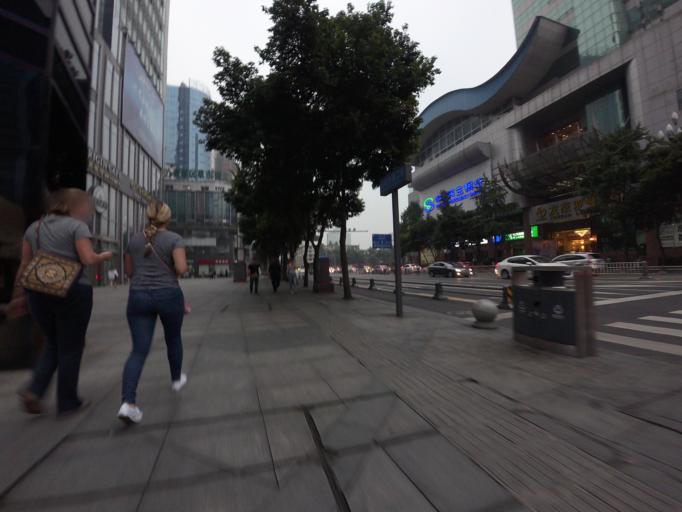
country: CN
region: Sichuan
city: Chengdu
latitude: 30.6712
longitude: 104.0634
